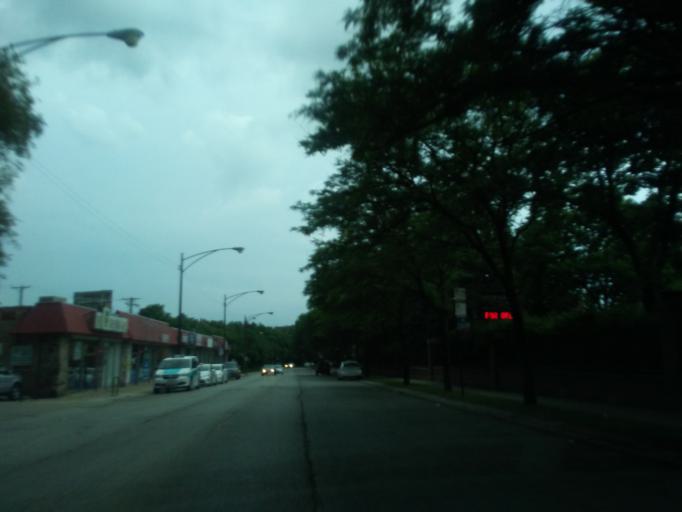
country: US
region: Illinois
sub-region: Cook County
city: Evanston
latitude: 41.9964
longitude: -87.6762
